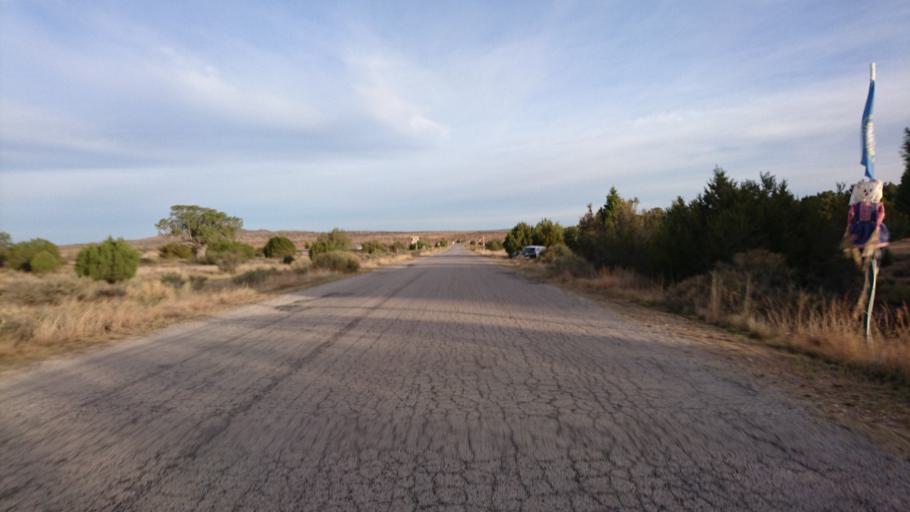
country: US
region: Arizona
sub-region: Mohave County
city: Peach Springs
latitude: 35.5239
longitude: -113.2279
